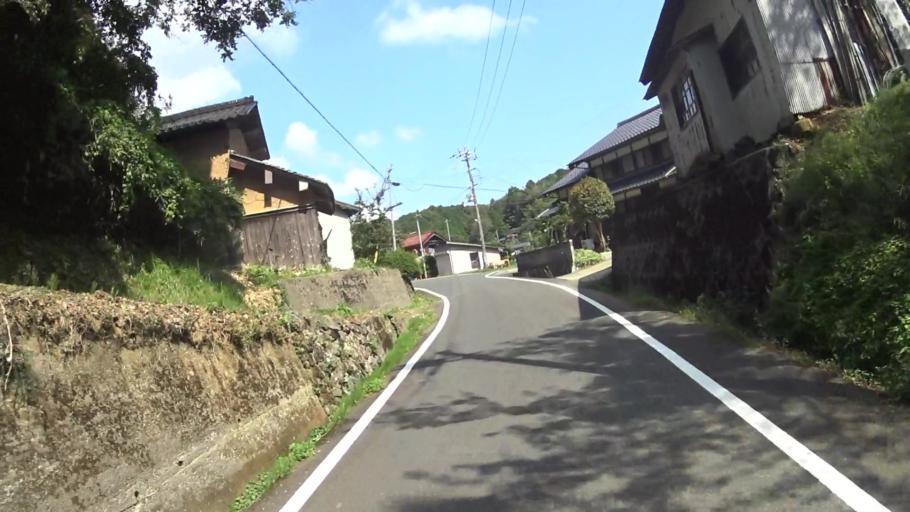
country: JP
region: Kyoto
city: Miyazu
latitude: 35.6812
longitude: 135.2669
